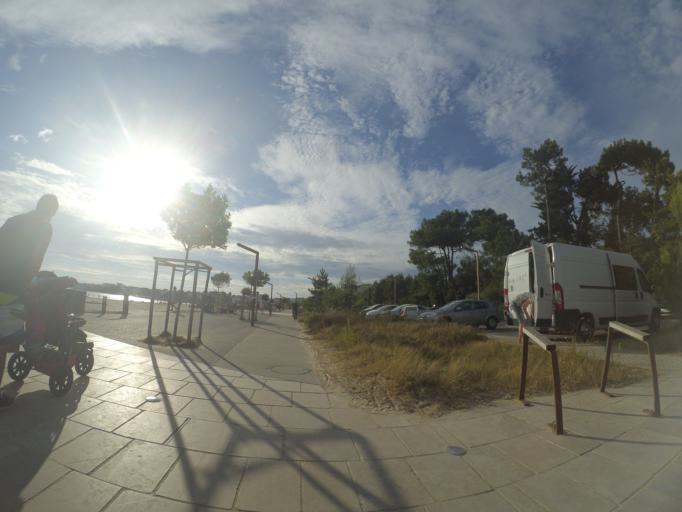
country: FR
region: Poitou-Charentes
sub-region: Departement de la Charente-Maritime
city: Saint-Georges-de-Didonne
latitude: 45.6000
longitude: -0.9954
